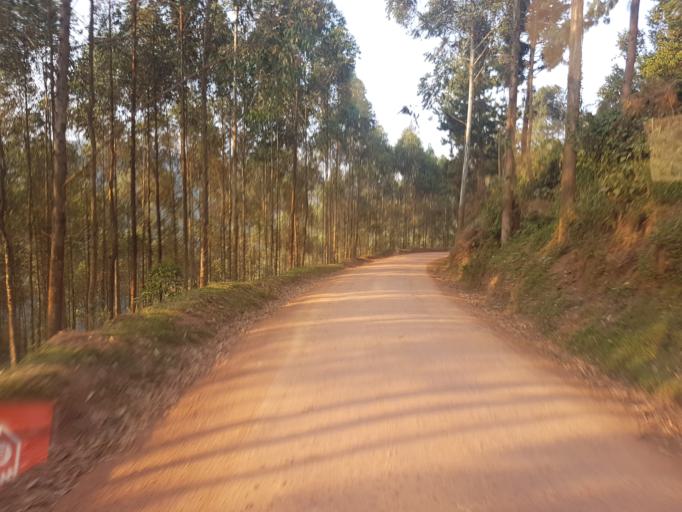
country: UG
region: Western Region
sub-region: Kabale District
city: Kabale
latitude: -1.1141
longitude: 29.9053
